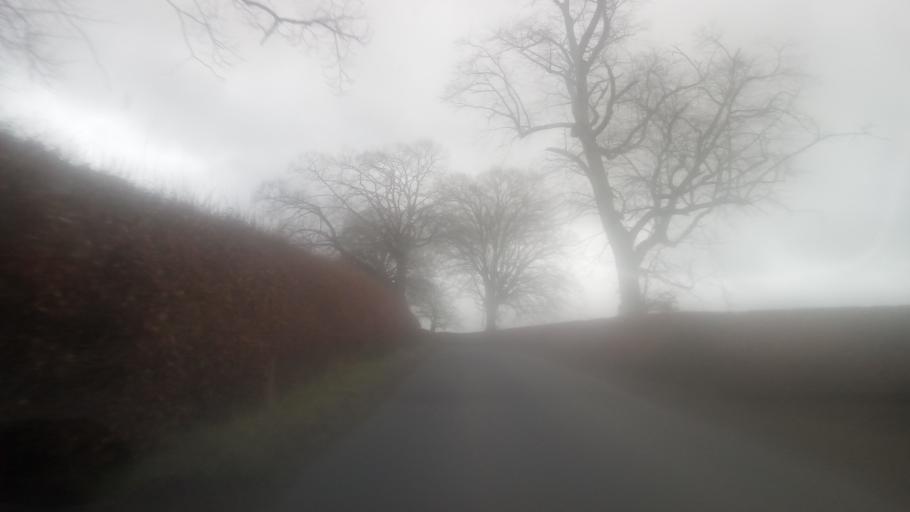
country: GB
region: Scotland
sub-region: The Scottish Borders
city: Jedburgh
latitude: 55.4775
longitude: -2.5254
